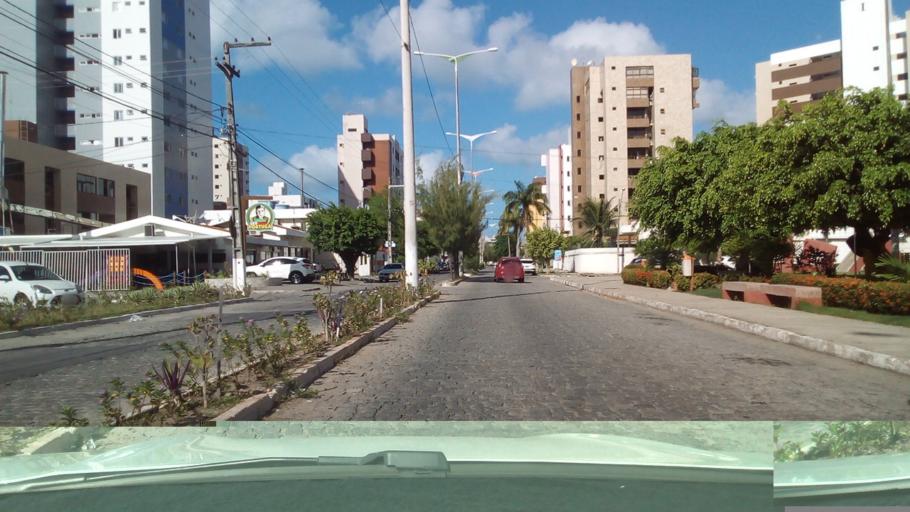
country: BR
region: Paraiba
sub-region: Joao Pessoa
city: Joao Pessoa
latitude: -7.0884
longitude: -34.8383
